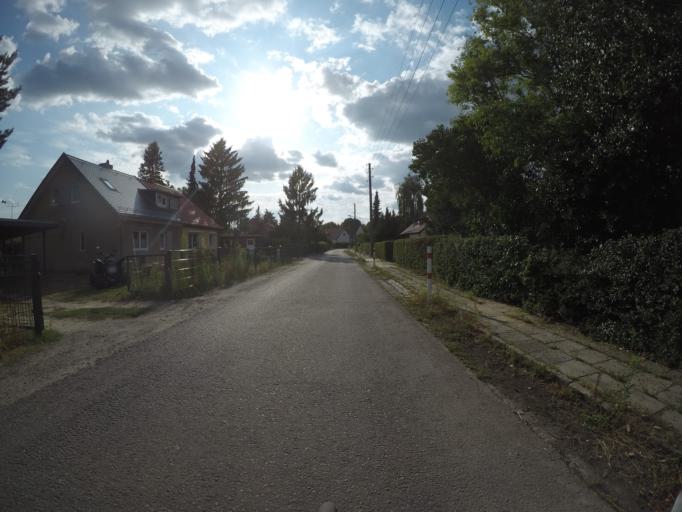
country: DE
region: Berlin
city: Hellersdorf
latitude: 52.5272
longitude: 13.6150
